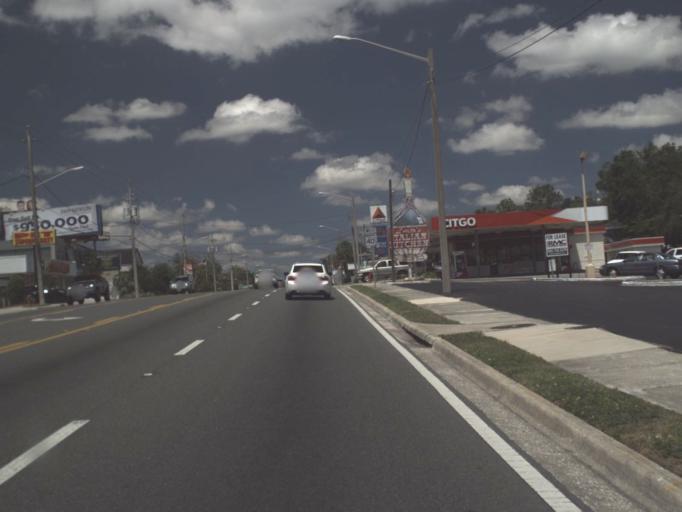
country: US
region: Florida
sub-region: Marion County
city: Ocala
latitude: 29.1870
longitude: -82.1128
